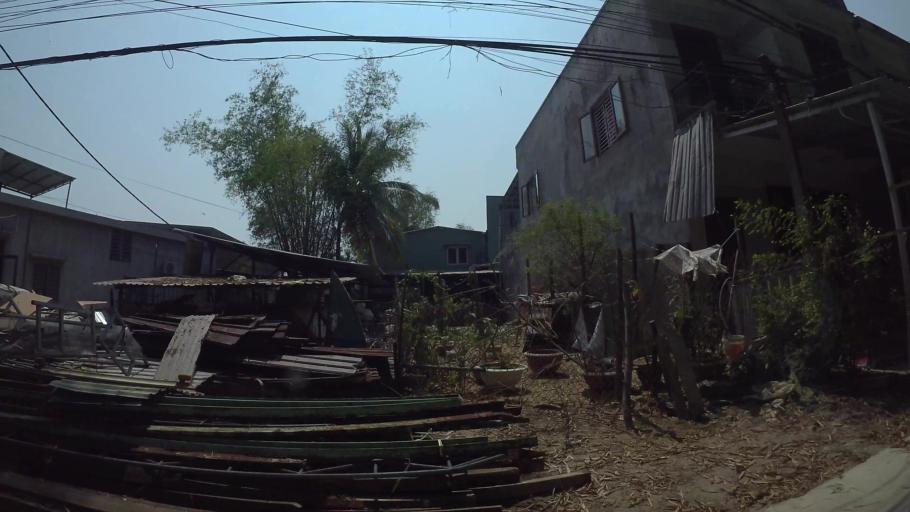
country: VN
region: Da Nang
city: Cam Le
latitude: 15.9970
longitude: 108.1935
